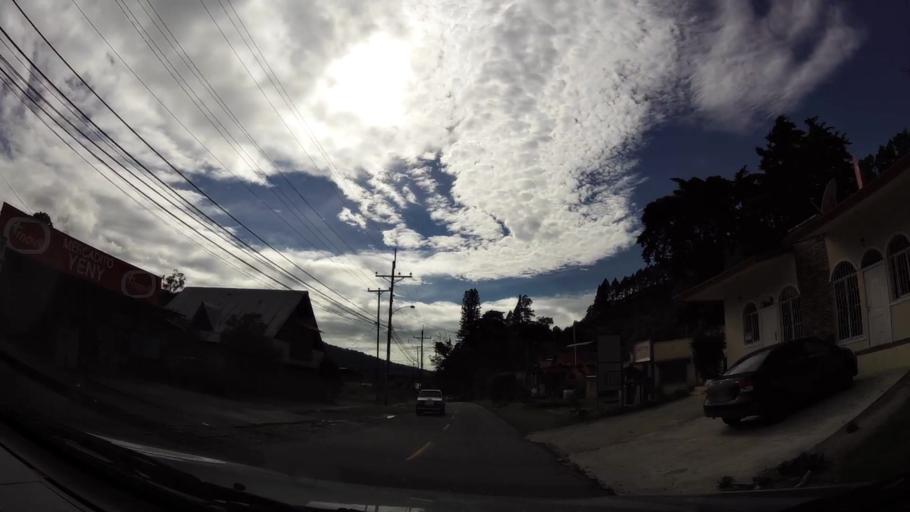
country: PA
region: Chiriqui
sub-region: Distrito Boquete
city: Boquete
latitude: 8.7913
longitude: -82.4413
